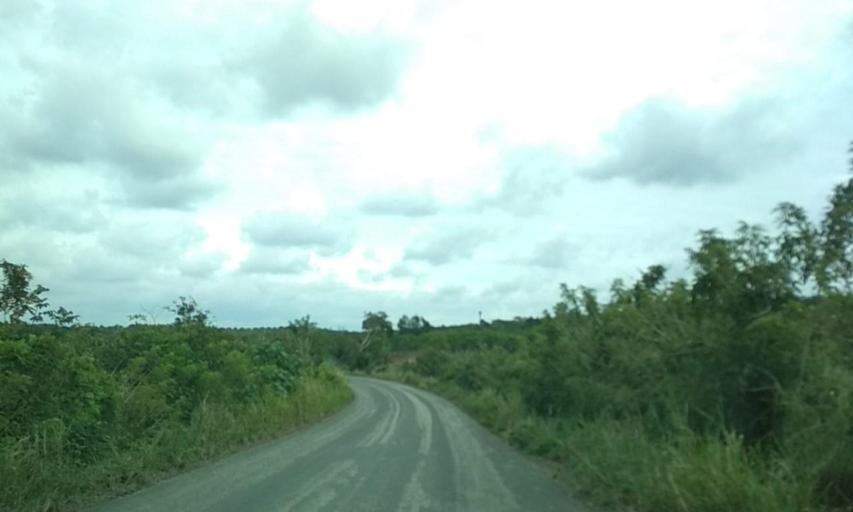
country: MX
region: Veracruz
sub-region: Papantla
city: El Chote
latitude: 20.3545
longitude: -97.3621
